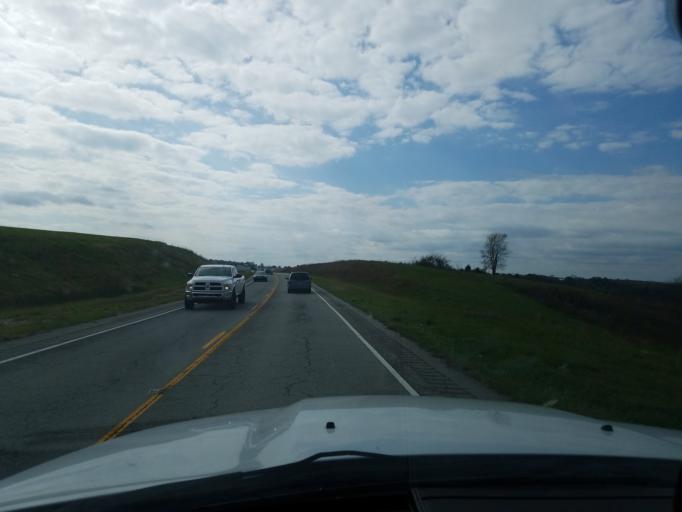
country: US
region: Kentucky
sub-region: Nelson County
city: Bardstown
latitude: 37.9219
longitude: -85.4706
